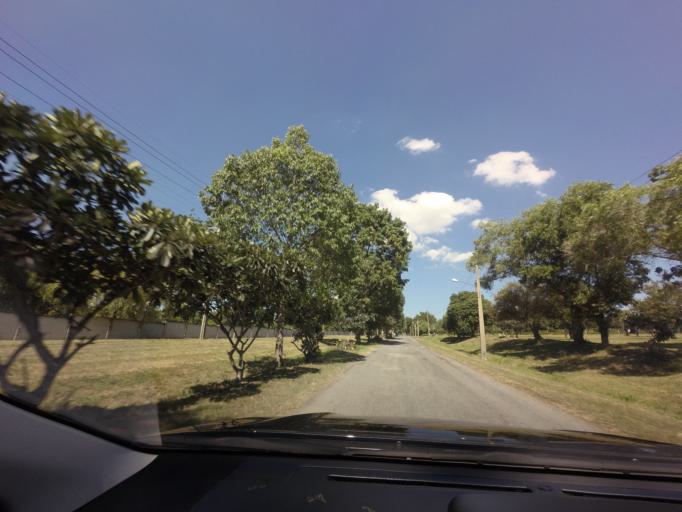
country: TH
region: Chon Buri
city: Bang Lamung
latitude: 13.1050
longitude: 100.9274
